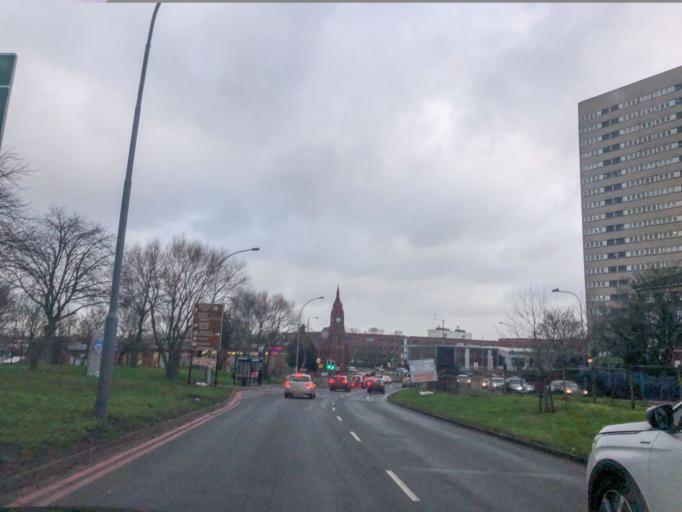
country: GB
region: England
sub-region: City and Borough of Birmingham
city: Hockley
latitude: 52.4839
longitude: -1.9214
